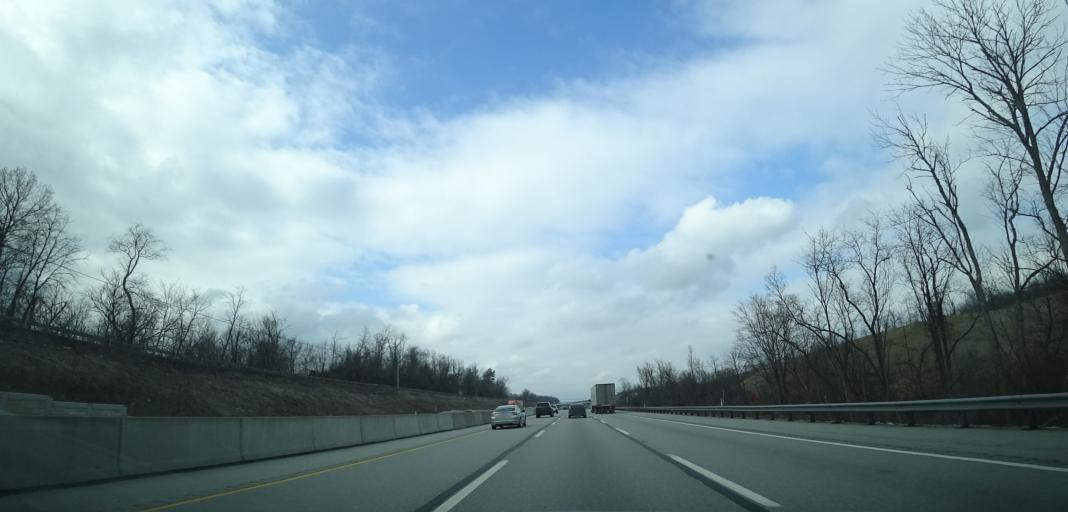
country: US
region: Pennsylvania
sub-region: Westmoreland County
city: Manor
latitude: 40.2805
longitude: -79.6689
